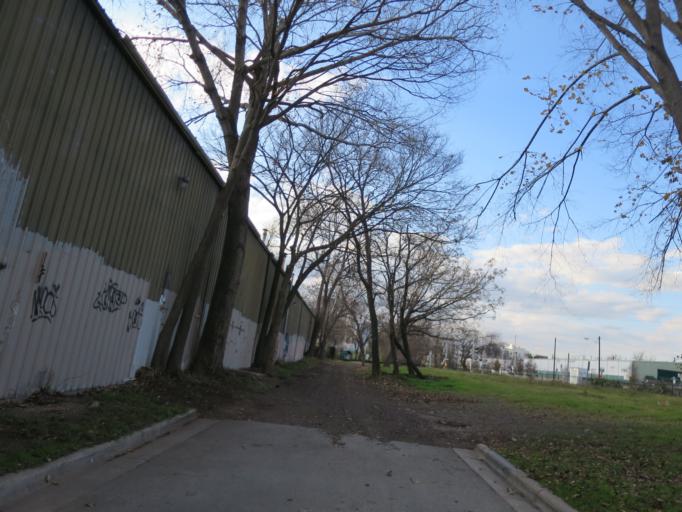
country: US
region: Texas
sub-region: Travis County
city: Austin
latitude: 30.2620
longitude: -97.7282
